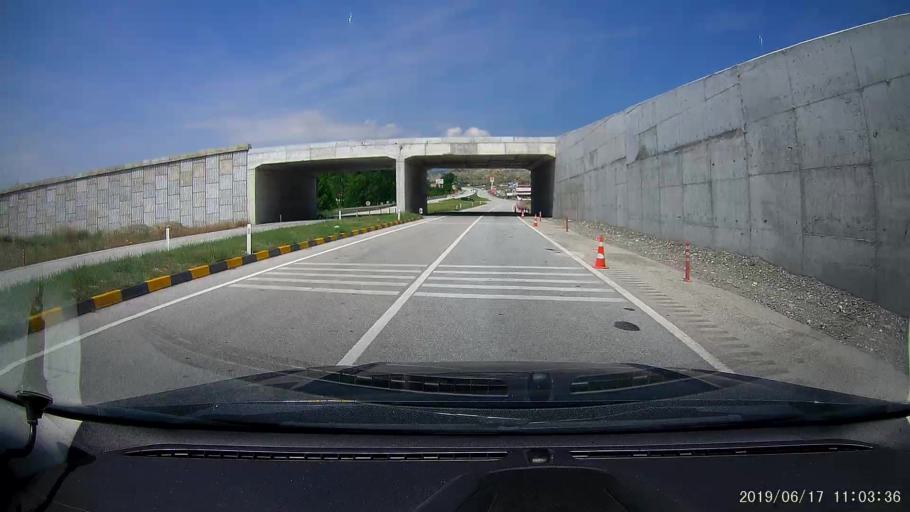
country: TR
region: Kastamonu
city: Tosya
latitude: 41.0184
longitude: 34.1128
